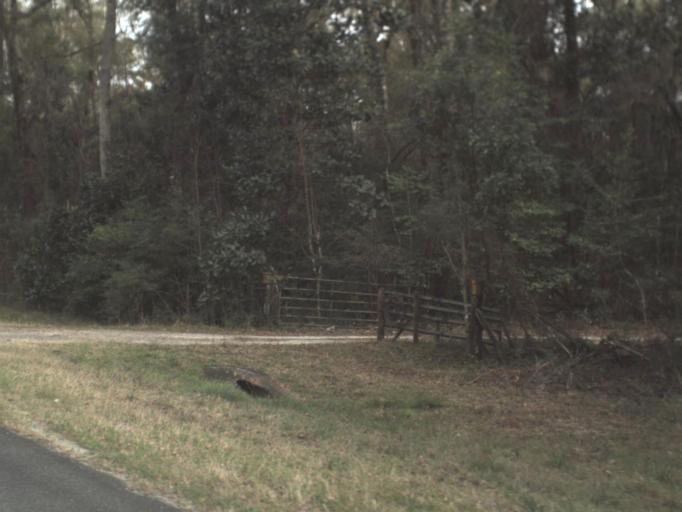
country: US
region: Florida
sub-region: Leon County
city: Woodville
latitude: 30.2429
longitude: -84.2857
